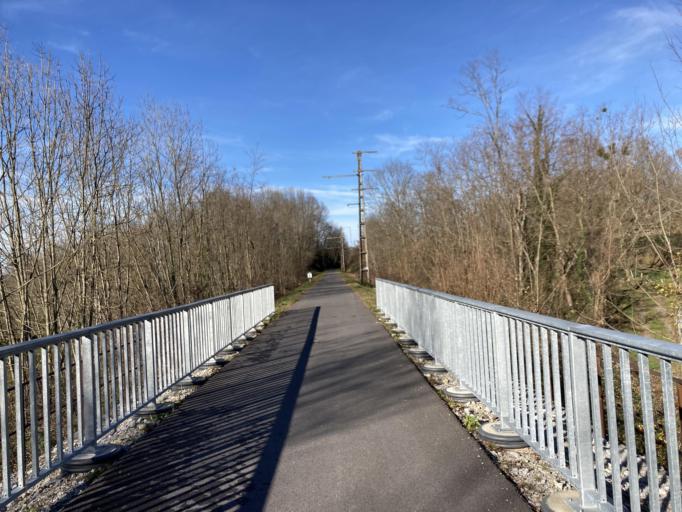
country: FR
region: Aquitaine
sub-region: Departement des Pyrenees-Atlantiques
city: Arudy
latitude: 43.1336
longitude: -0.4454
